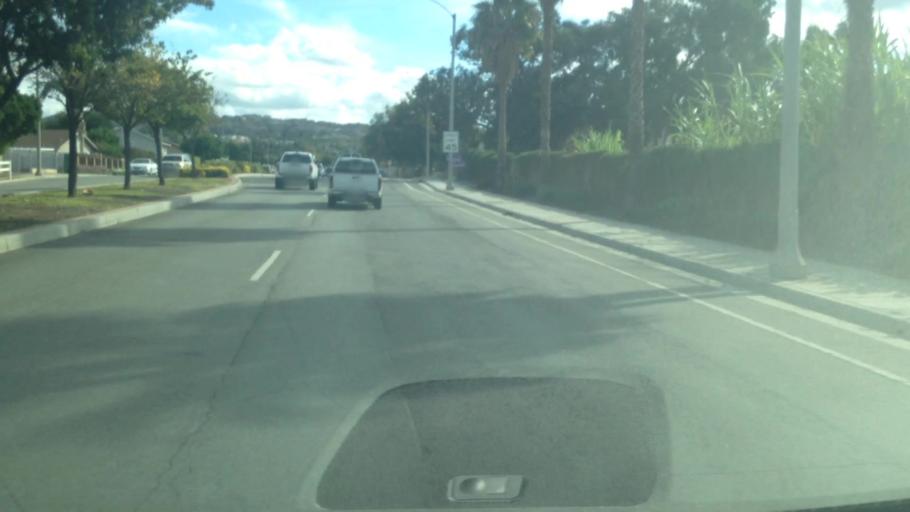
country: US
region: California
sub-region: Riverside County
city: Home Gardens
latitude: 33.8904
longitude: -117.4656
